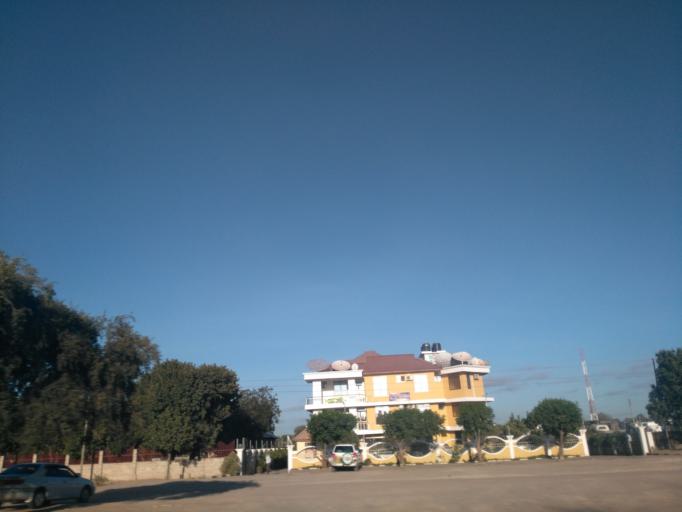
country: TZ
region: Dodoma
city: Dodoma
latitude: -6.1611
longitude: 35.7466
